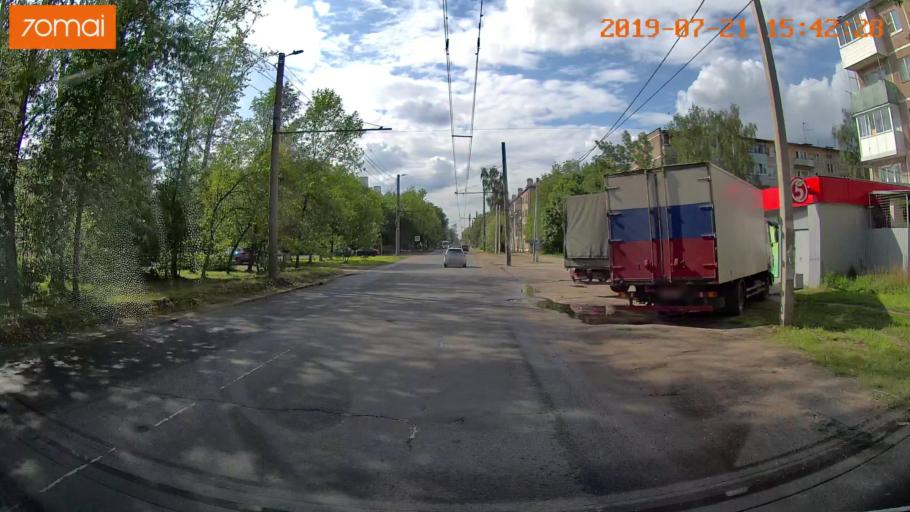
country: RU
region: Ivanovo
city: Kokhma
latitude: 56.9736
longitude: 41.0535
